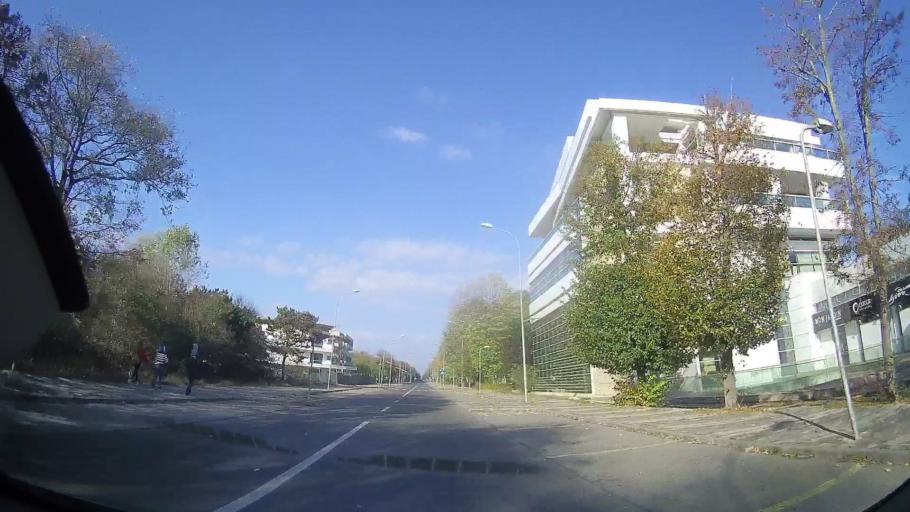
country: RO
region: Constanta
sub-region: Comuna Douazeci si Trei August
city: Douazeci si Trei August
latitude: 43.8779
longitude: 28.6030
